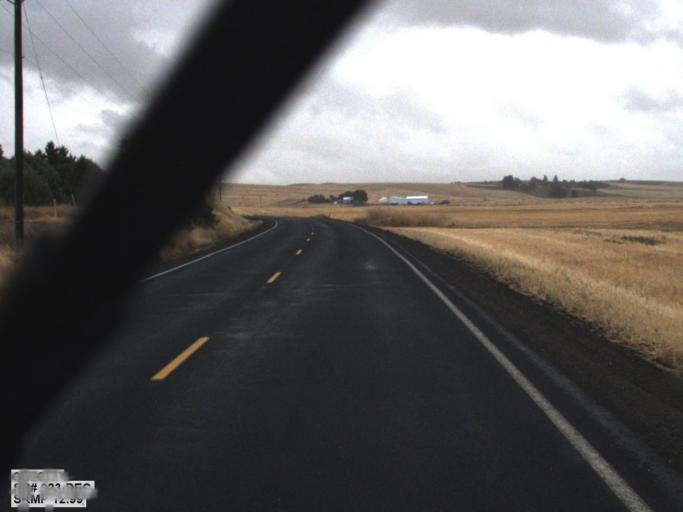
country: US
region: Washington
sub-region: Whitman County
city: Colfax
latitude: 47.0872
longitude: -117.5578
